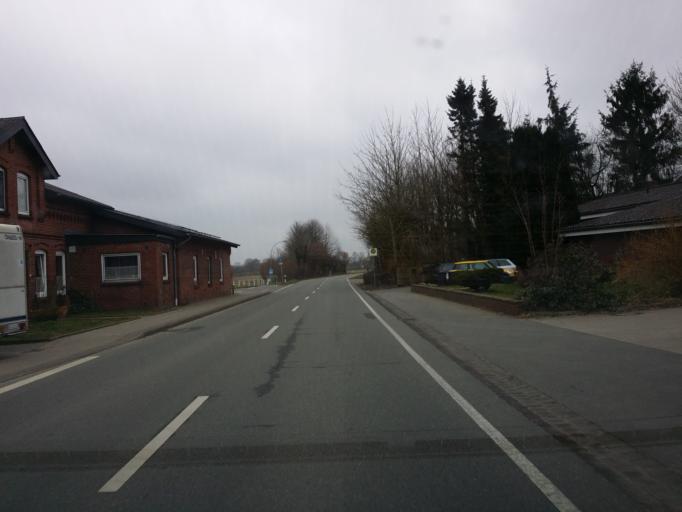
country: DE
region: Schleswig-Holstein
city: Hassmoor
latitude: 54.3136
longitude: 9.7847
